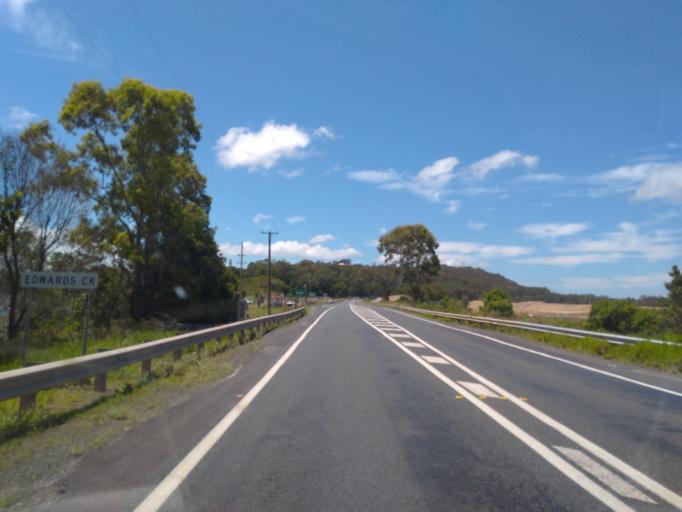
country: AU
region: New South Wales
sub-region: Clarence Valley
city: Maclean
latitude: -29.4746
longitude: 153.2050
